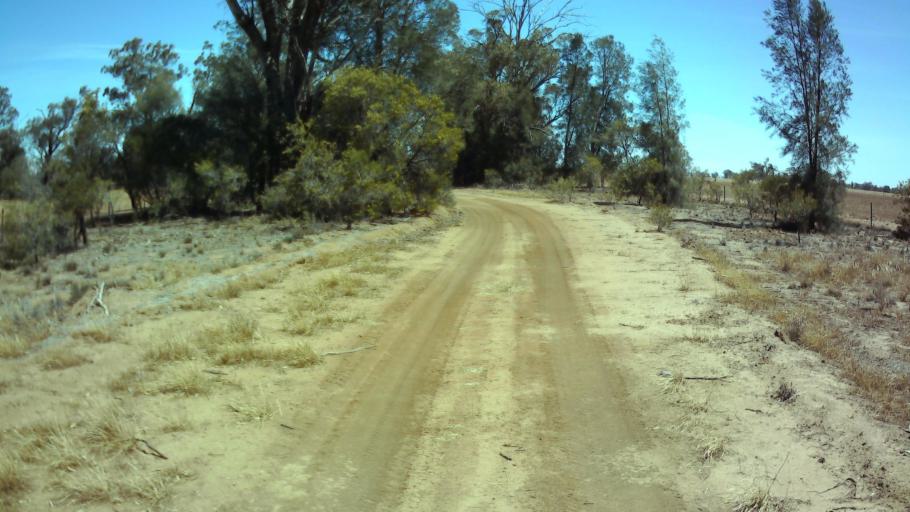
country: AU
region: New South Wales
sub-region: Bland
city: West Wyalong
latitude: -33.9238
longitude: 147.6822
